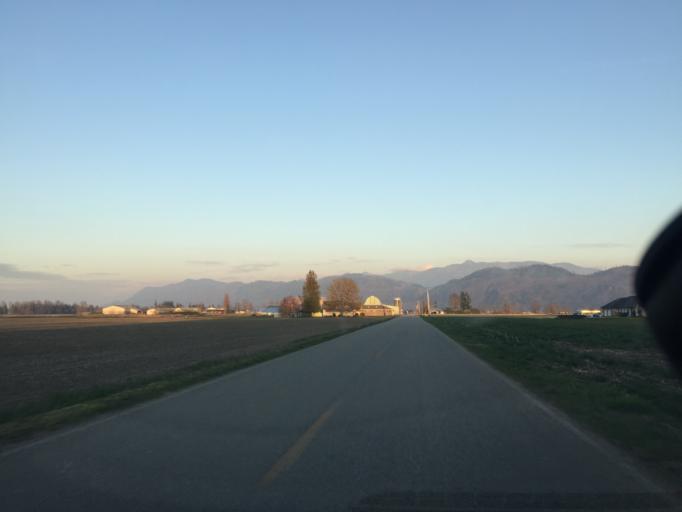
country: US
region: Washington
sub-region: Whatcom County
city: Sumas
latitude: 49.0001
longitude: -122.2487
